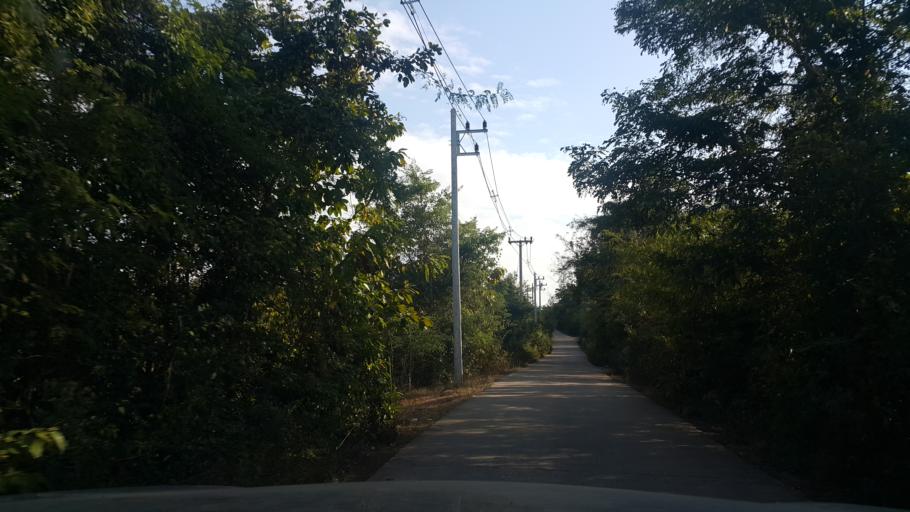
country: TH
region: Lampang
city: Hang Chat
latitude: 18.3037
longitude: 99.3518
